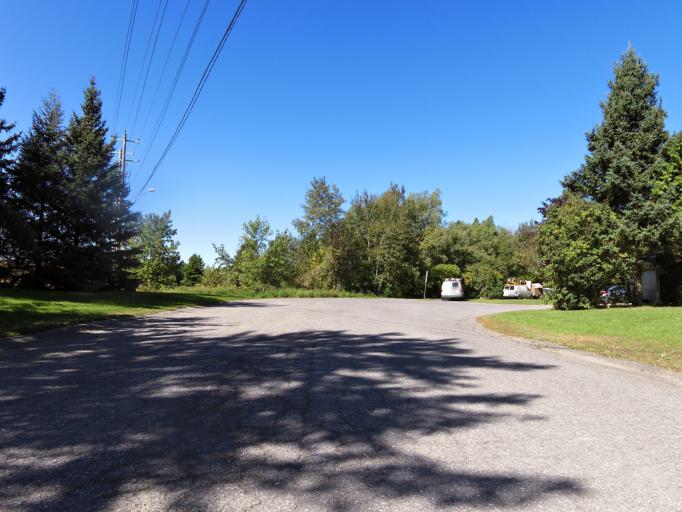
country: CA
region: Ontario
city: Casselman
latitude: 45.2677
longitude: -75.2808
